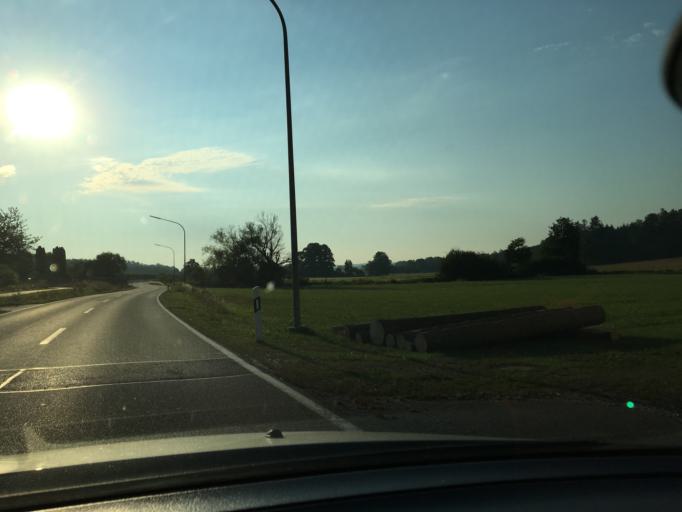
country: DE
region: Bavaria
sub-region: Lower Bavaria
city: Vilsbiburg
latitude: 48.5002
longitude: 12.3592
